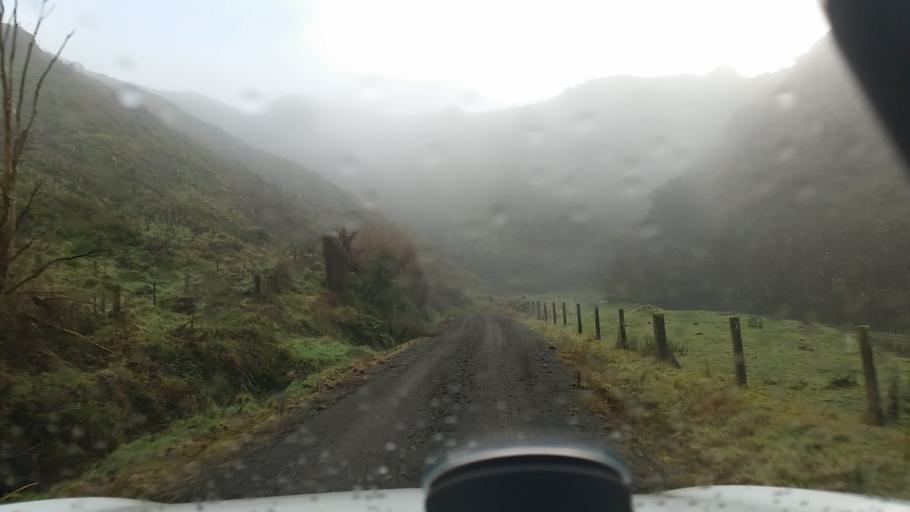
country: NZ
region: Taranaki
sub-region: South Taranaki District
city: Eltham
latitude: -39.4152
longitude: 174.4272
